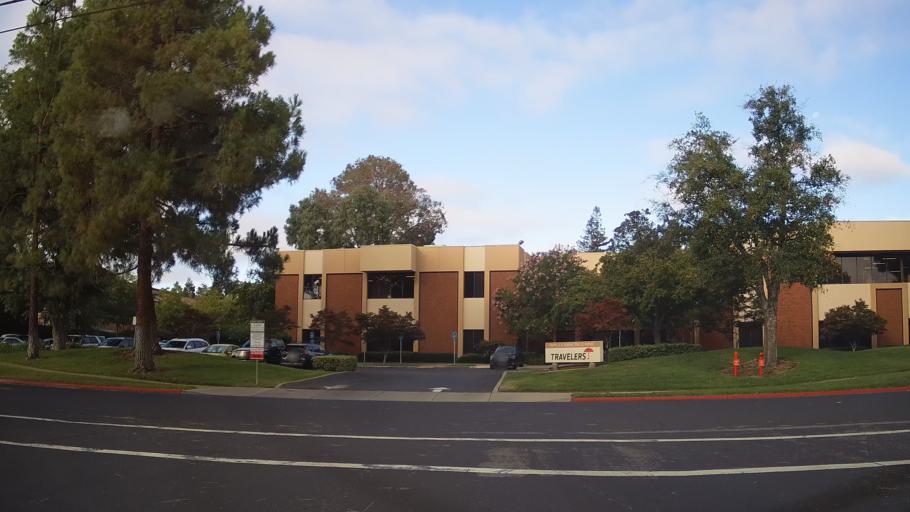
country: US
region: California
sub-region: Contra Costa County
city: Waldon
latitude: 37.9285
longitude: -122.0304
